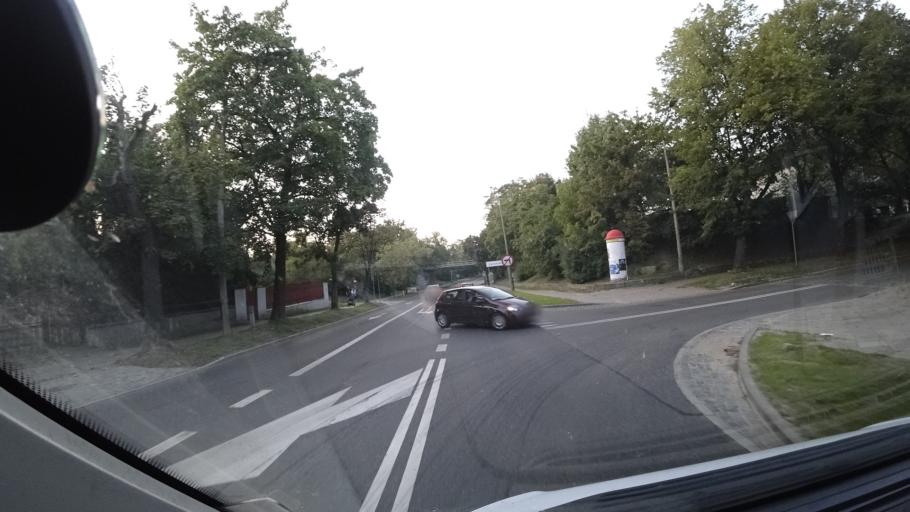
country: PL
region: Silesian Voivodeship
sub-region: Zabrze
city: Zabrze
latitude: 50.3021
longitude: 18.7620
